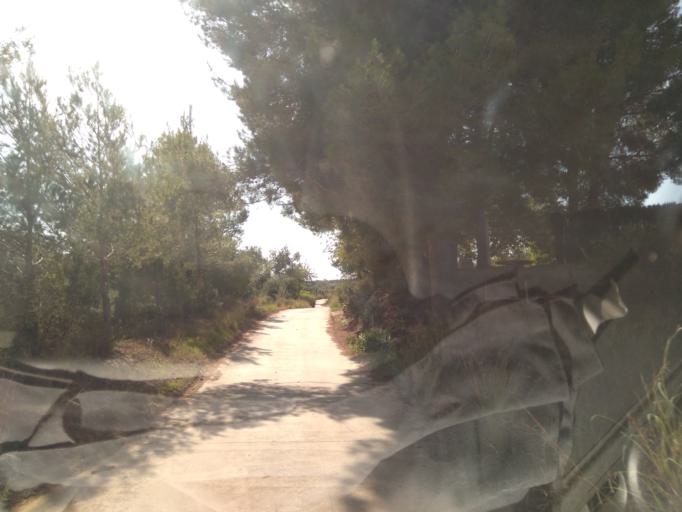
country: ES
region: Valencia
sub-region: Provincia de Valencia
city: Tous
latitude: 39.1776
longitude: -0.6032
